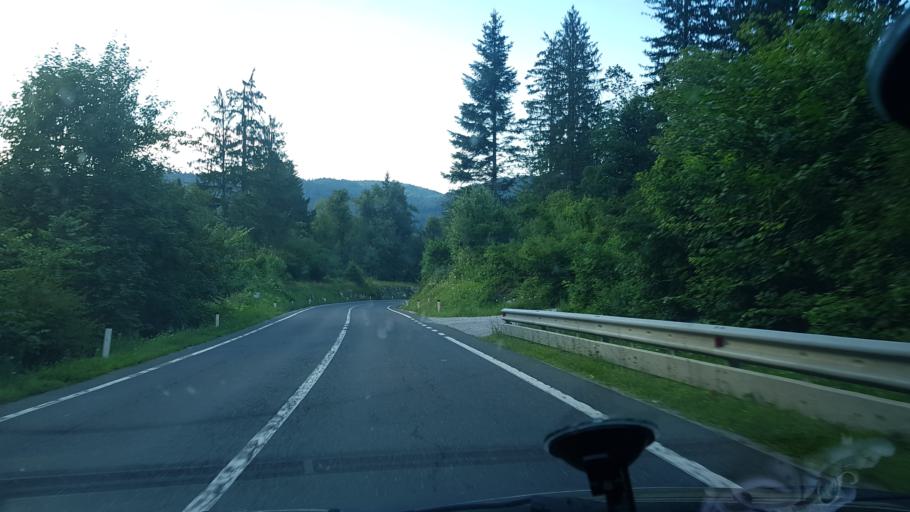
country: SI
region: Vrhnika
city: Vrhnika
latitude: 45.9499
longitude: 14.2533
